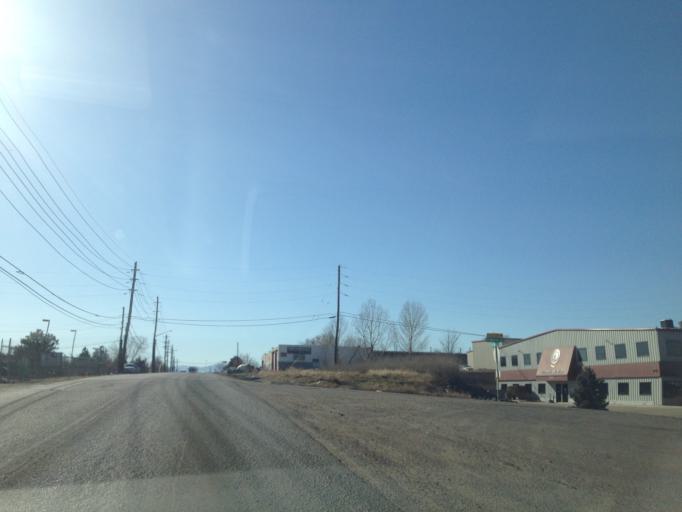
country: US
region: Colorado
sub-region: Adams County
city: Welby
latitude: 39.8019
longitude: -104.9712
